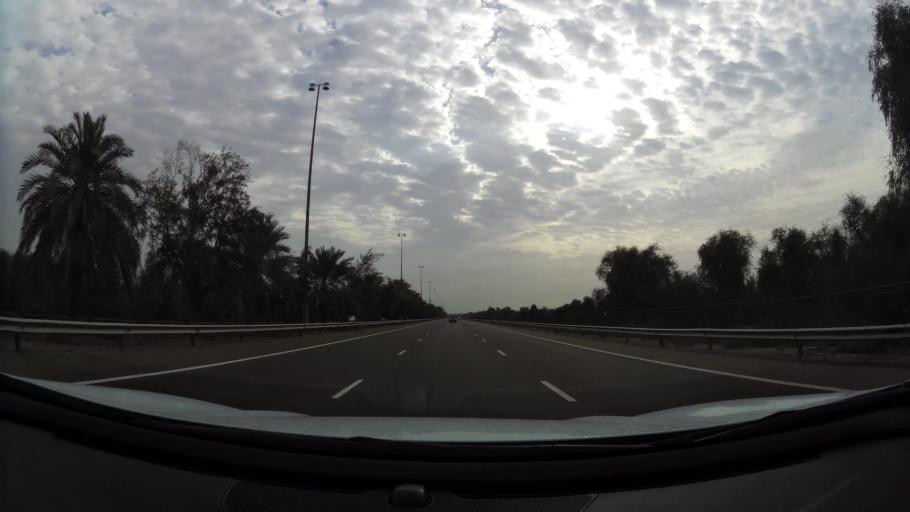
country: AE
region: Abu Dhabi
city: Al Ain
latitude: 24.1793
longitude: 55.1678
